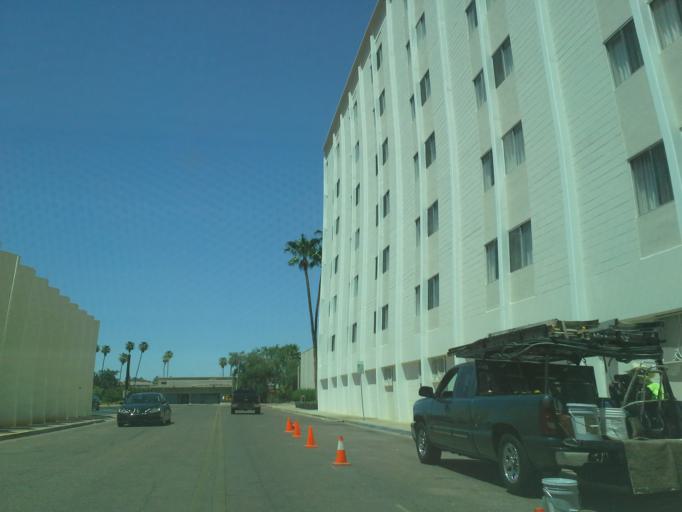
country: US
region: Arizona
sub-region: Maricopa County
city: Phoenix
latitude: 33.4919
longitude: -112.0765
